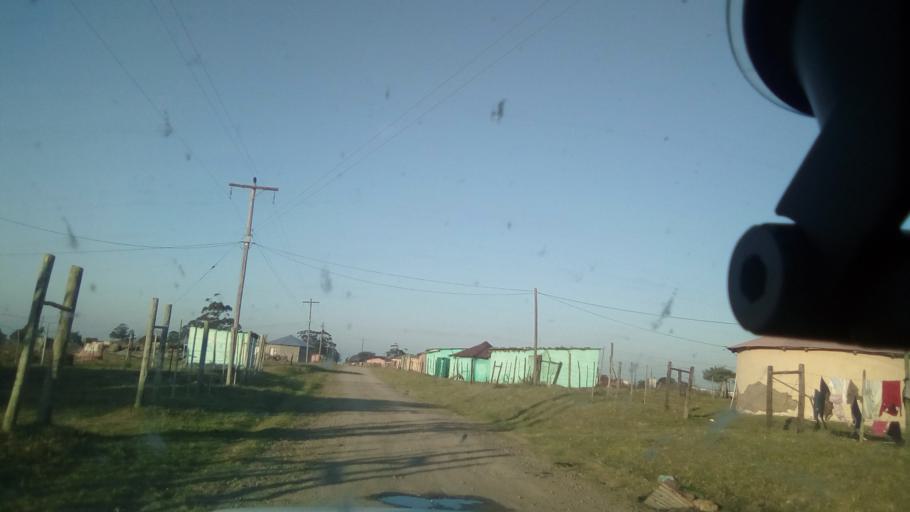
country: ZA
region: Eastern Cape
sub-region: Buffalo City Metropolitan Municipality
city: Bhisho
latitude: -32.9721
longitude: 27.2946
